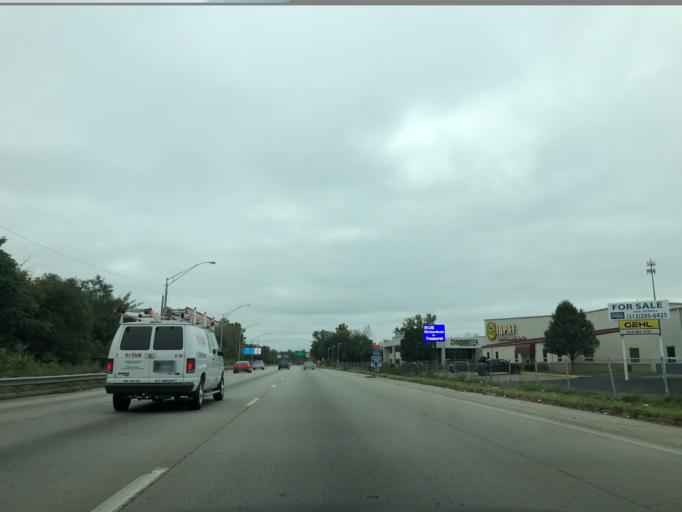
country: US
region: Ohio
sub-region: Hamilton County
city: Lockland
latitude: 39.2234
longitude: -84.4549
